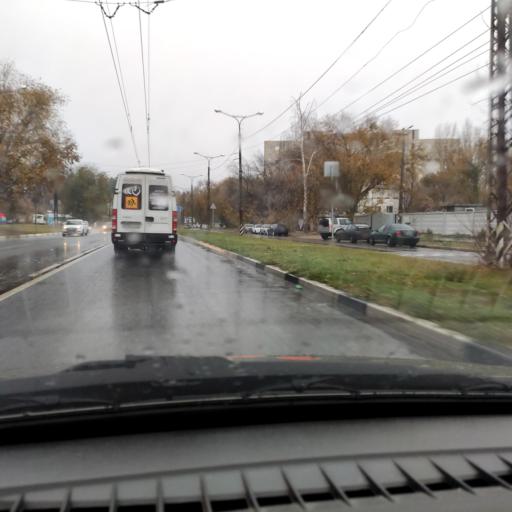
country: RU
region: Samara
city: Tol'yatti
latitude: 53.4987
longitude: 49.4017
